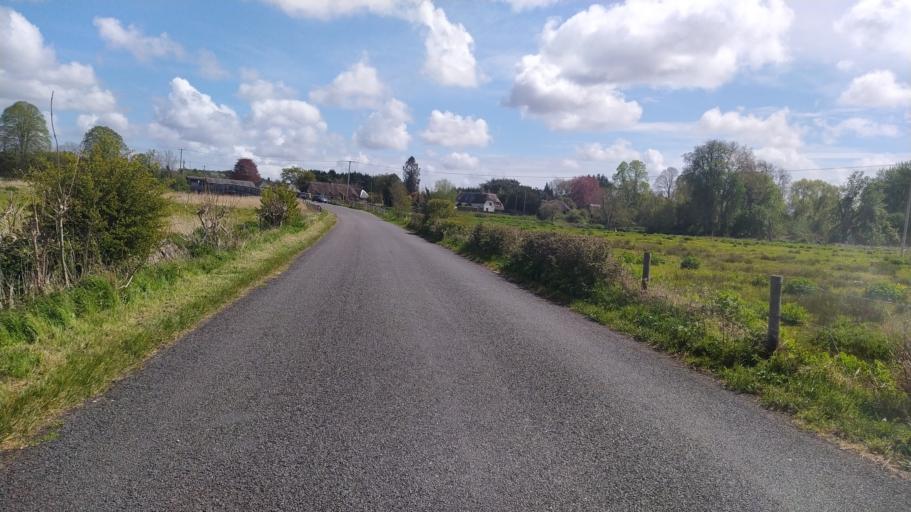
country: GB
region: England
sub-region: Hampshire
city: Fordingbridge
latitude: 50.8873
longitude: -1.7903
